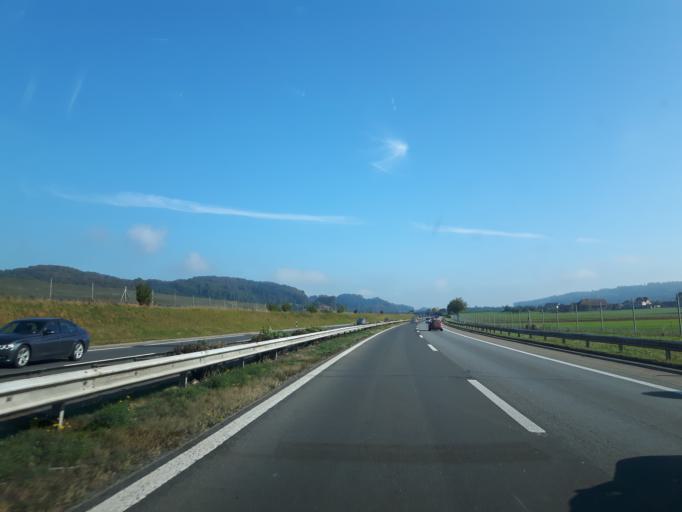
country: CH
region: Lucerne
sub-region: Willisau District
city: Wauwil
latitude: 47.2073
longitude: 8.0306
